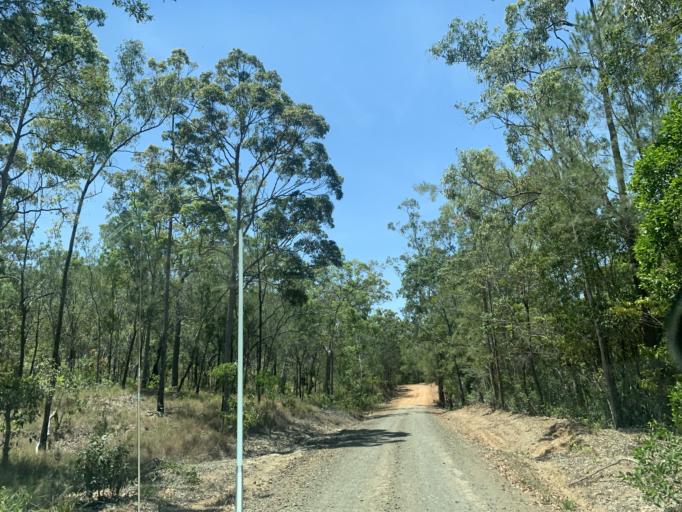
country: AU
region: Queensland
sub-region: Cairns
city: Redlynch
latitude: -16.9296
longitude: 145.6021
